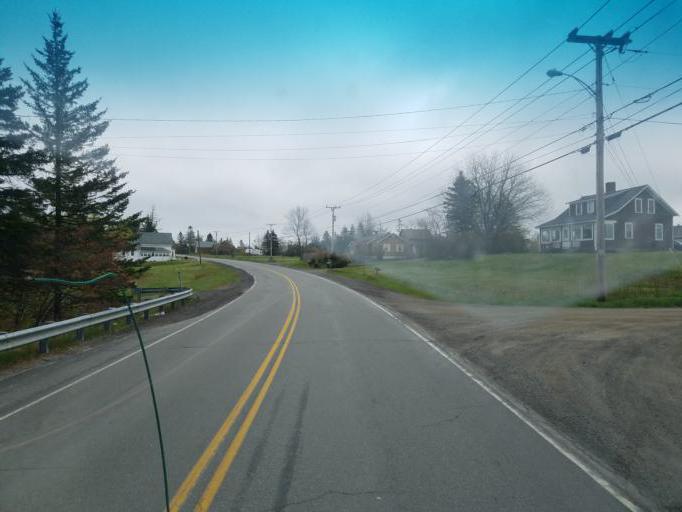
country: US
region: Maine
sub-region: Washington County
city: Eastport
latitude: 44.8216
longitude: -67.0497
